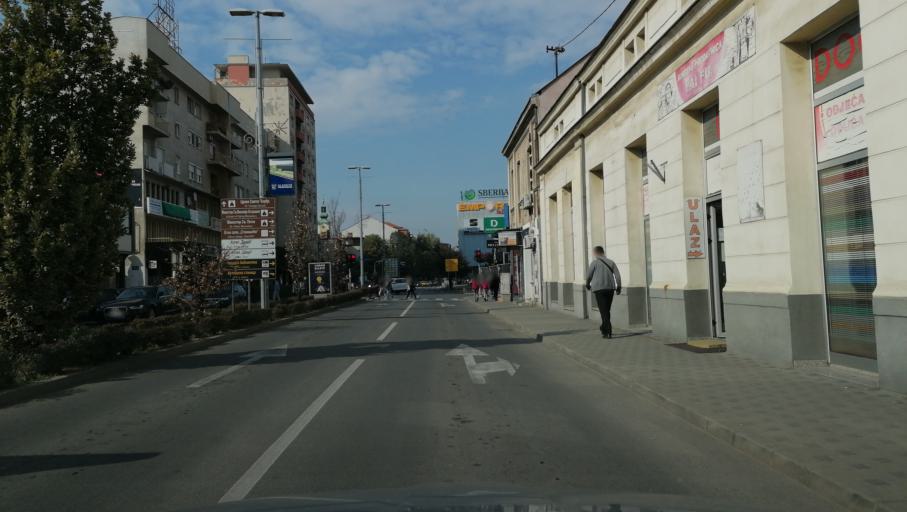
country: BA
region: Republika Srpska
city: Bijeljina
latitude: 44.7556
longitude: 19.2163
